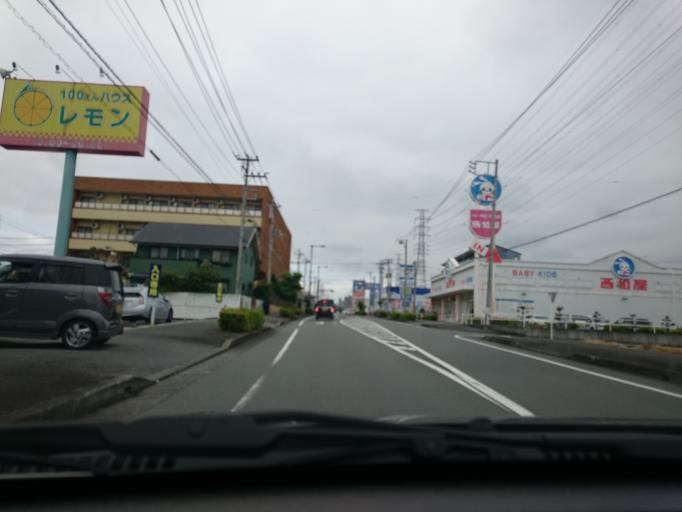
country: JP
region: Shizuoka
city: Mishima
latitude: 35.1529
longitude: 138.9046
